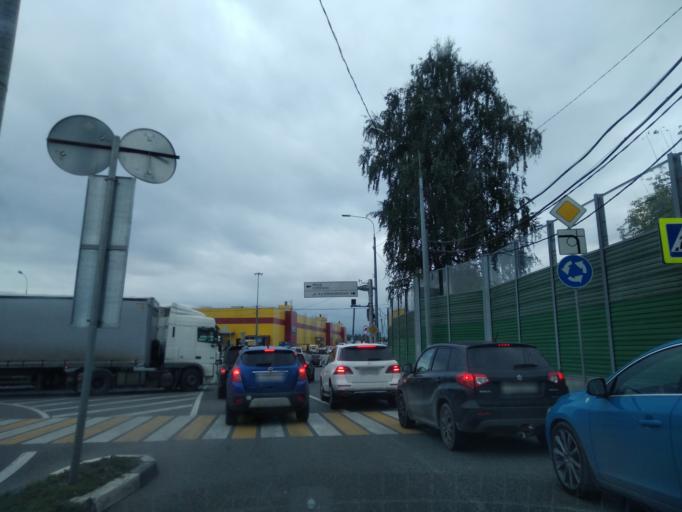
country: RU
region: Moskovskaya
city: Pavshino
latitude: 55.8100
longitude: 37.3809
